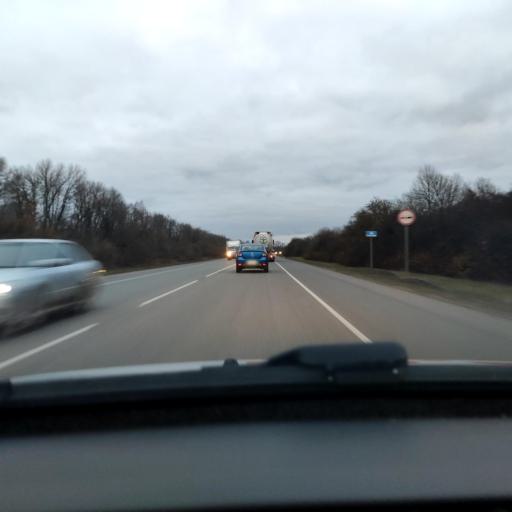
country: RU
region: Lipetsk
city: Borinskoye
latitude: 52.4508
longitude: 39.2957
